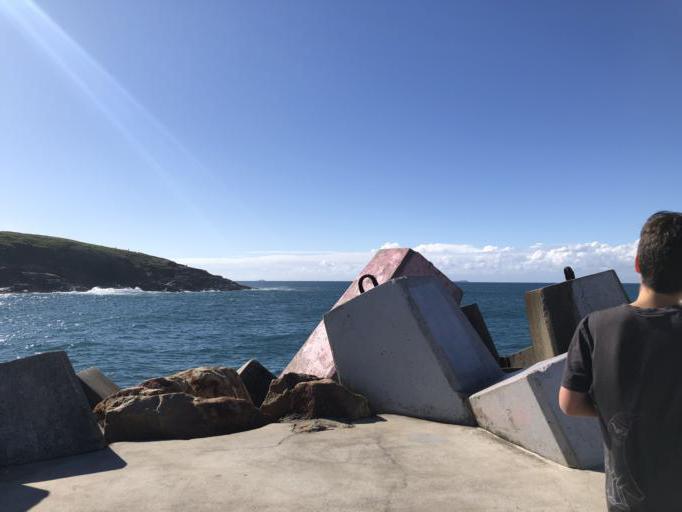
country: AU
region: New South Wales
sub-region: Coffs Harbour
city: Coffs Harbour
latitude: -30.3092
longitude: 153.1527
